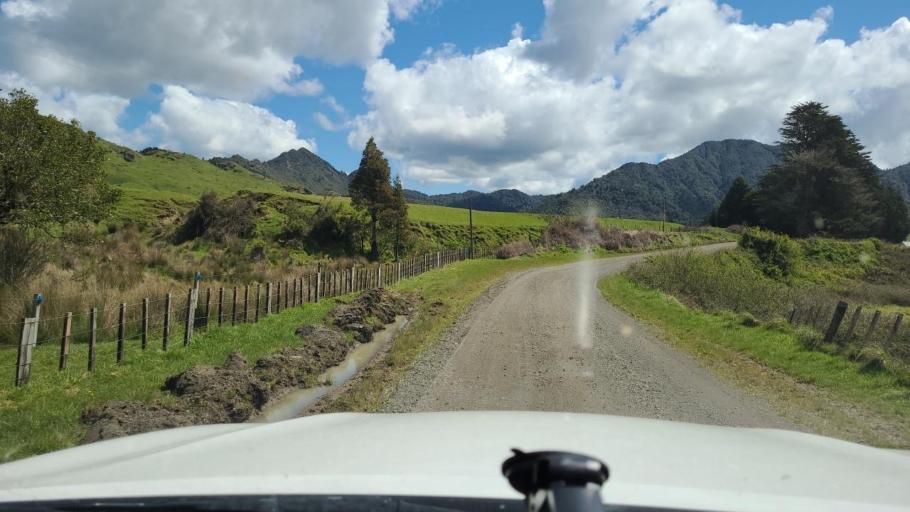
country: NZ
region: Bay of Plenty
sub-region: Opotiki District
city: Opotiki
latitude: -38.2819
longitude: 177.5234
